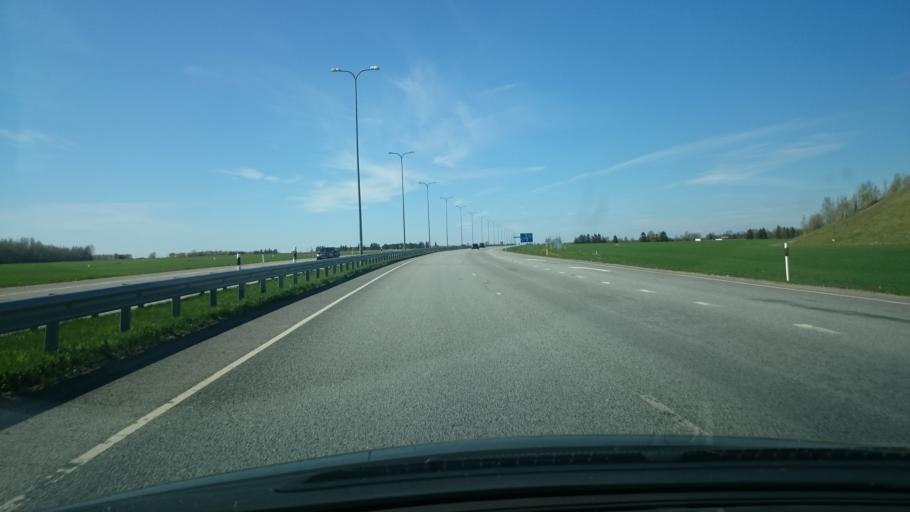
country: EE
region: Ida-Virumaa
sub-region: Kohtla-Jaerve linn
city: Kohtla-Jarve
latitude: 59.3911
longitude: 27.3384
